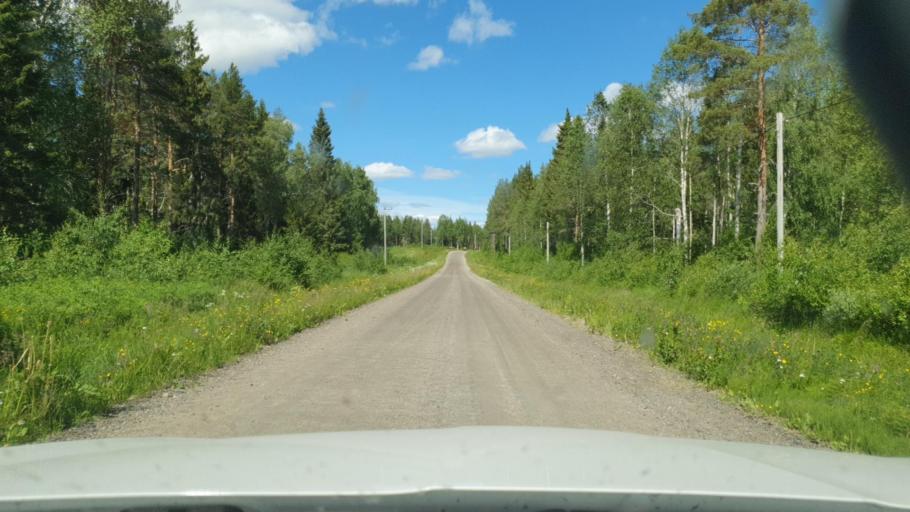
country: SE
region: Vaesterbotten
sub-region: Skelleftea Kommun
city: Backa
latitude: 65.1511
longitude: 21.1630
